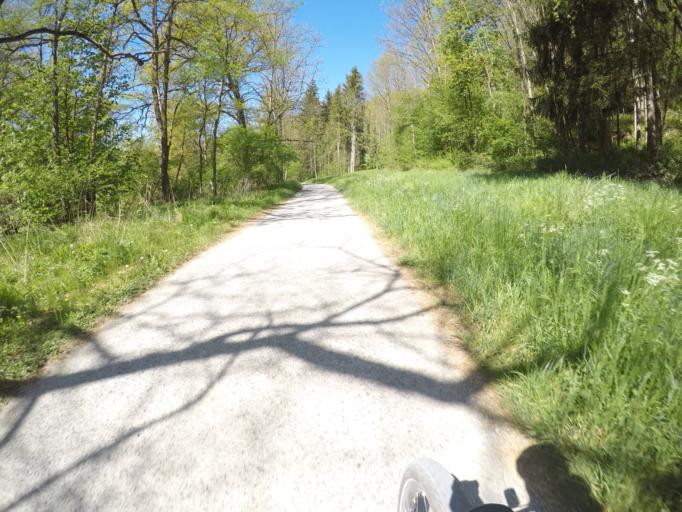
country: DE
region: Baden-Wuerttemberg
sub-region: Regierungsbezirk Stuttgart
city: Waiblingen
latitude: 48.8692
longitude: 9.3055
